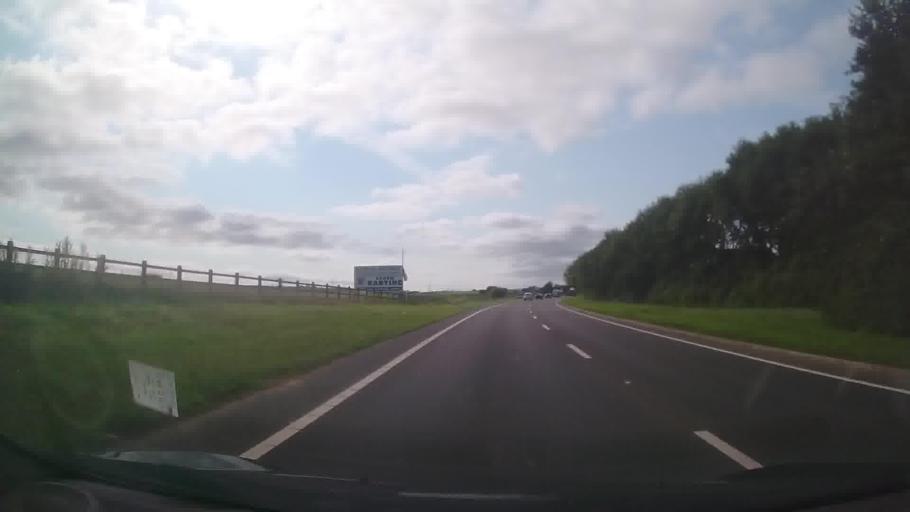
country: GB
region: Wales
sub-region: Pembrokeshire
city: Manorbier
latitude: 51.6935
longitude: -4.8127
